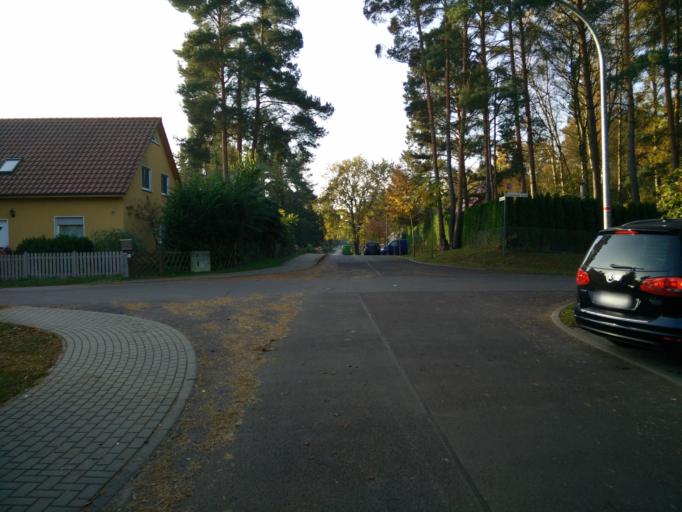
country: DE
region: Brandenburg
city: Falkensee
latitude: 52.5824
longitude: 13.0915
